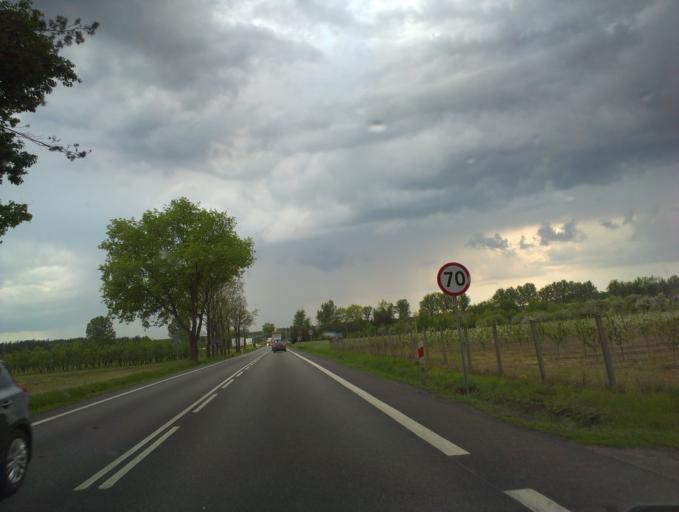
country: PL
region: Masovian Voivodeship
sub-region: Powiat grojecki
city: Pniewy
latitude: 51.9317
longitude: 20.6365
